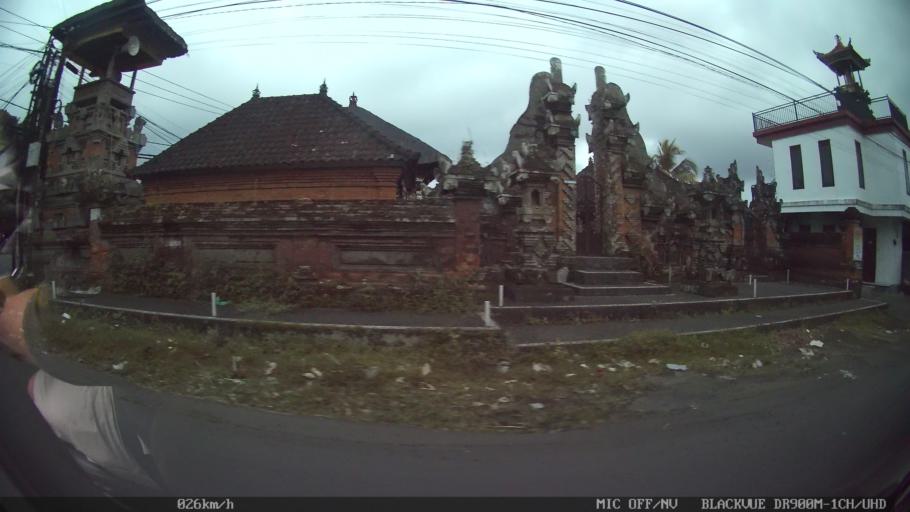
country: ID
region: Bali
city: Banjar Triwangsakeliki
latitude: -8.4478
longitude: 115.2629
